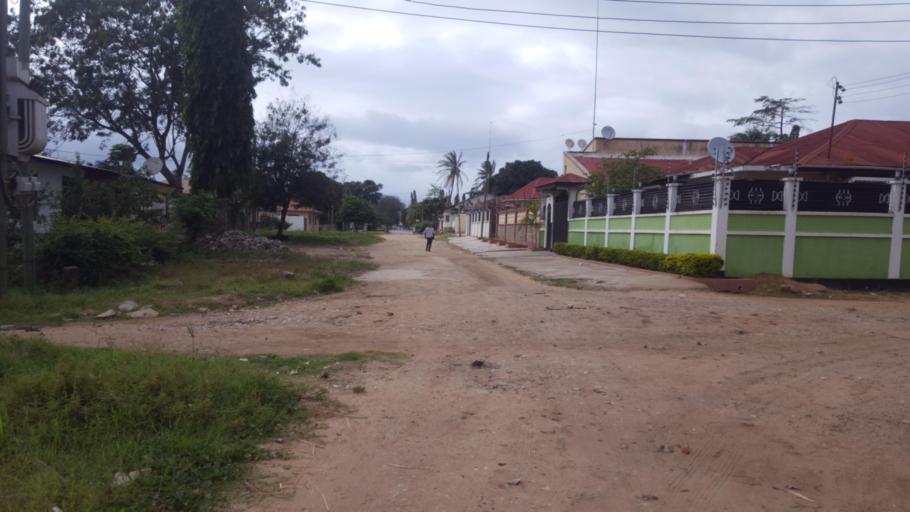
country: TZ
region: Tanga
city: Tanga
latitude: -5.0692
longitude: 39.0949
